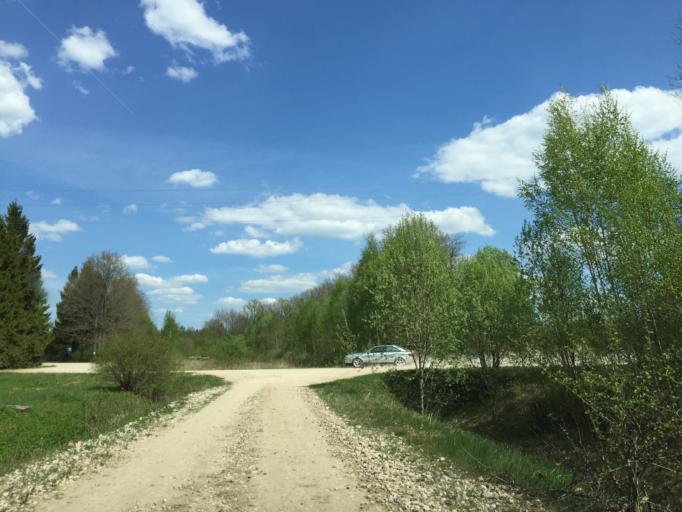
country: LV
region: Limbazu Rajons
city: Limbazi
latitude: 57.4099
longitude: 24.6189
